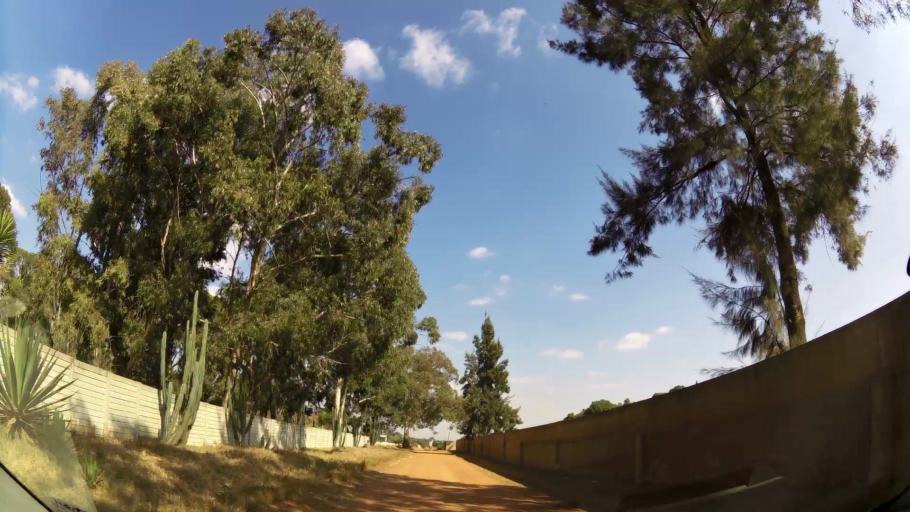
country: ZA
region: Gauteng
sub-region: Ekurhuleni Metropolitan Municipality
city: Benoni
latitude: -26.0796
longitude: 28.3492
